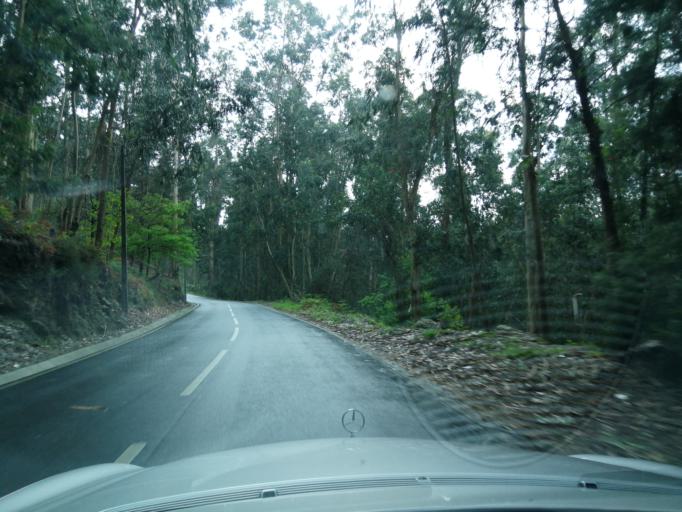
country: PT
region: Braga
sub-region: Braga
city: Oliveira
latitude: 41.4627
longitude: -8.4772
